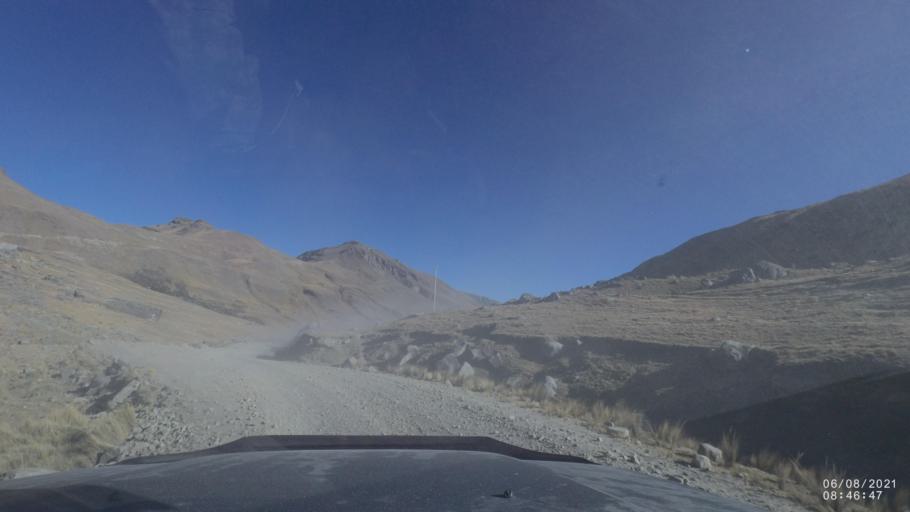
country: BO
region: Cochabamba
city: Sipe Sipe
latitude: -17.1675
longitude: -66.4220
